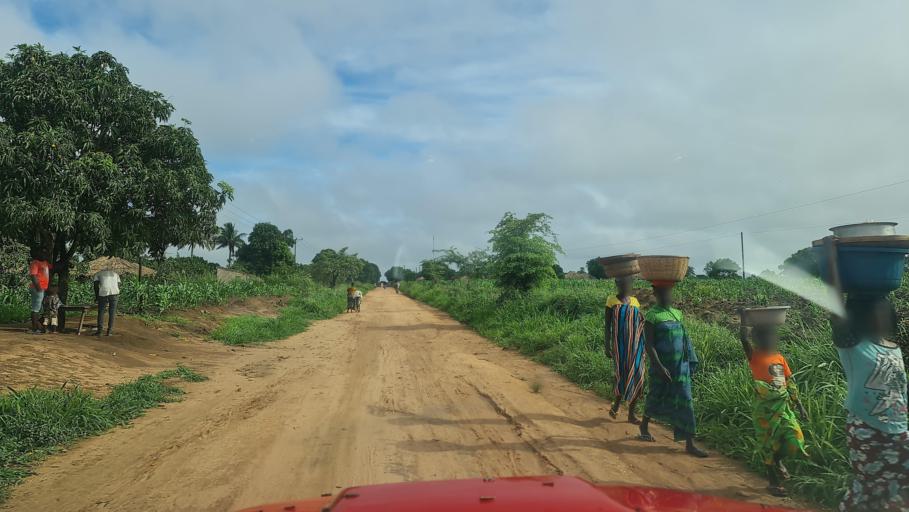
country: MW
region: Southern Region
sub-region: Nsanje District
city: Nsanje
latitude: -17.3050
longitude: 35.5932
